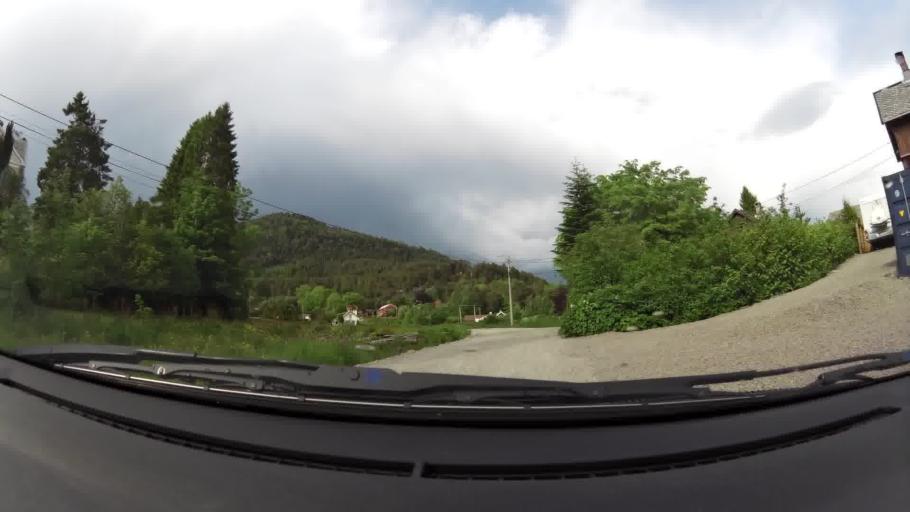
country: NO
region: More og Romsdal
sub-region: Kristiansund
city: Kristiansund
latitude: 63.0284
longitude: 7.7501
